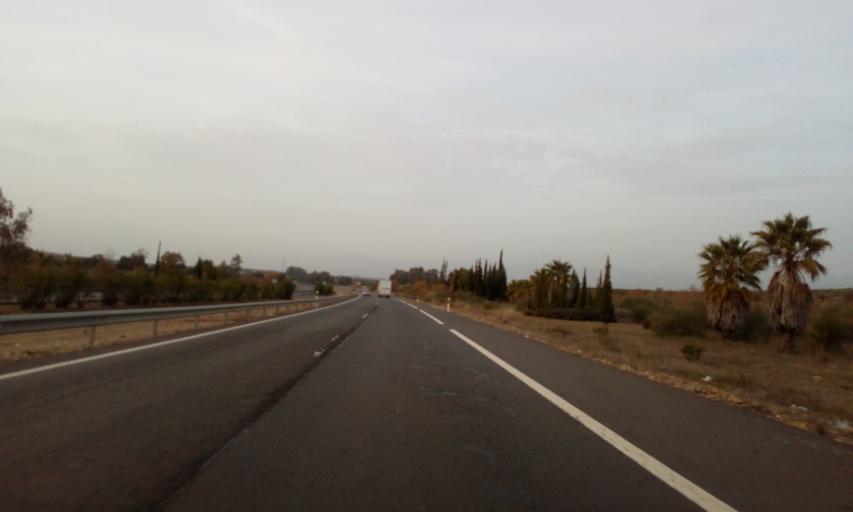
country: ES
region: Andalusia
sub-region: Provincia de Huelva
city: Gibraleon
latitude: 37.3454
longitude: -6.9239
